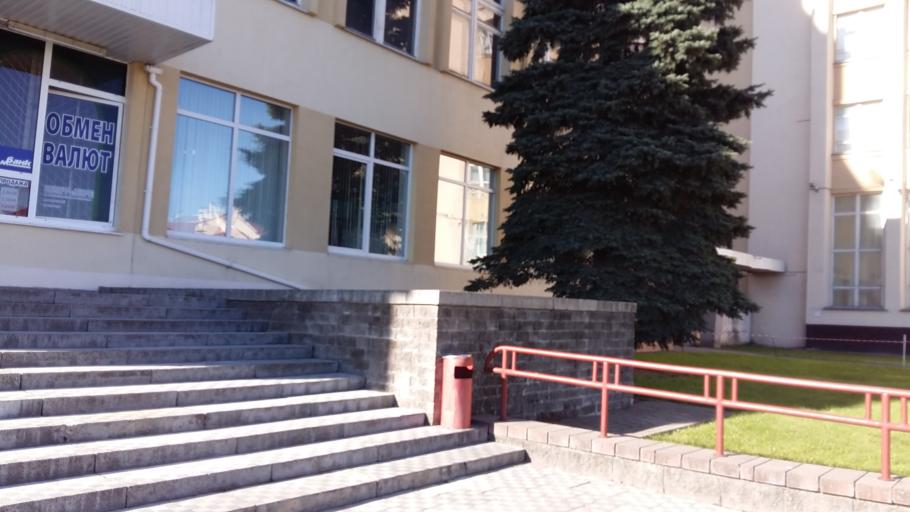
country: BY
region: Grodnenskaya
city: Hrodna
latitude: 53.6764
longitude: 23.8388
